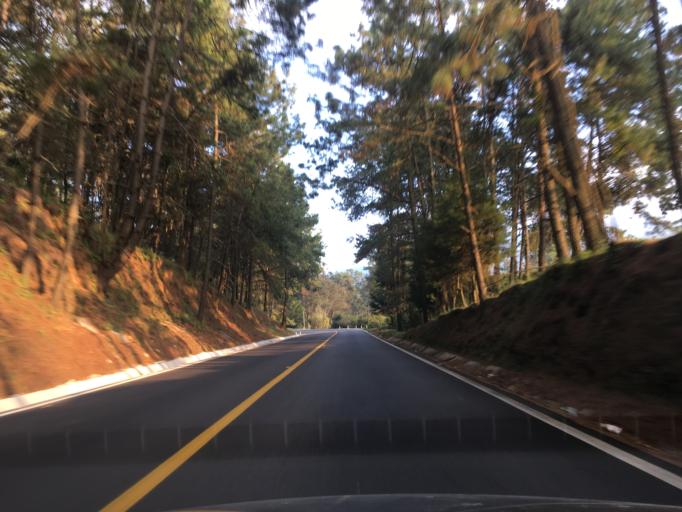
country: MX
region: Michoacan
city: Tingambato
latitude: 19.4924
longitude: -101.8203
